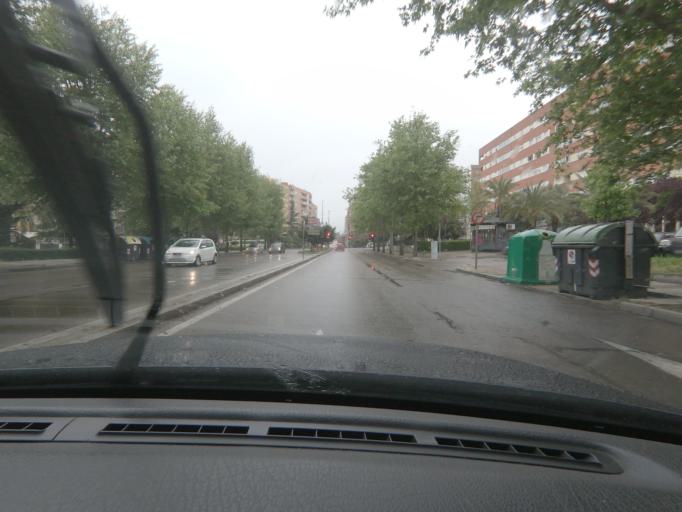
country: ES
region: Extremadura
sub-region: Provincia de Badajoz
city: Badajoz
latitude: 38.8682
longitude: -6.9730
